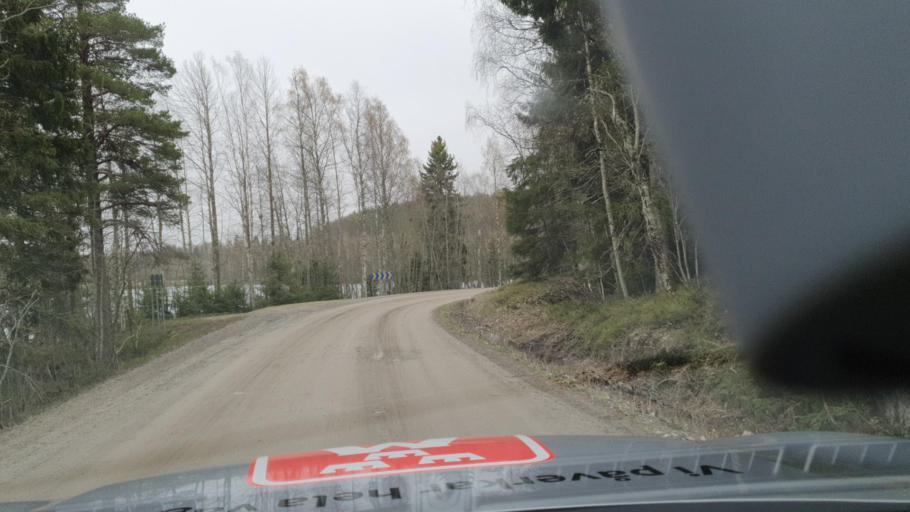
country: SE
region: Vaesternorrland
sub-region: OErnskoeldsviks Kommun
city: Husum
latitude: 63.6336
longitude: 19.0598
